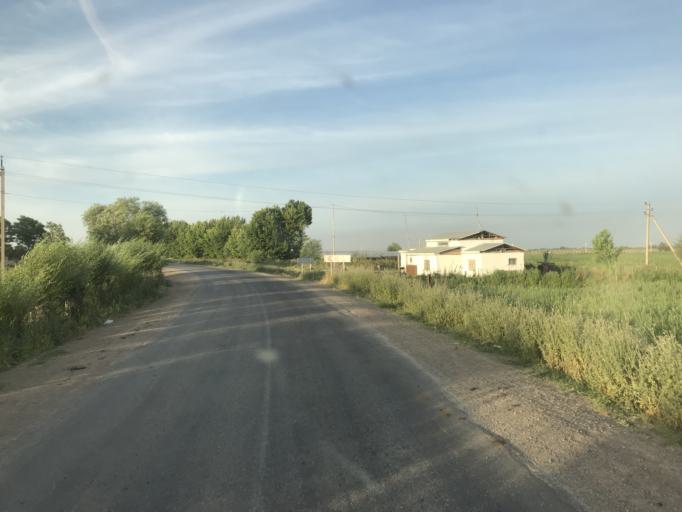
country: KZ
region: Ongtustik Qazaqstan
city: Asykata
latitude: 40.9537
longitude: 68.4609
